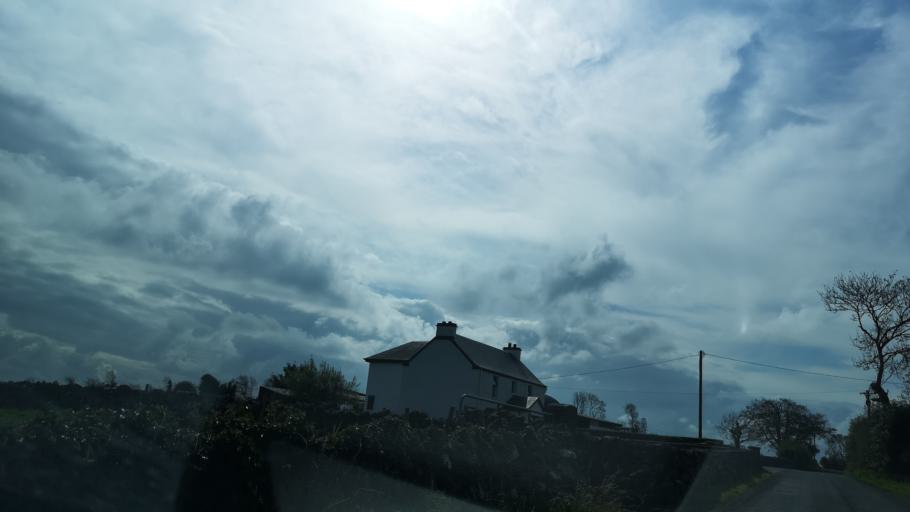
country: IE
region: Connaught
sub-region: County Galway
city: Athenry
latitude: 53.3055
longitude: -8.8112
